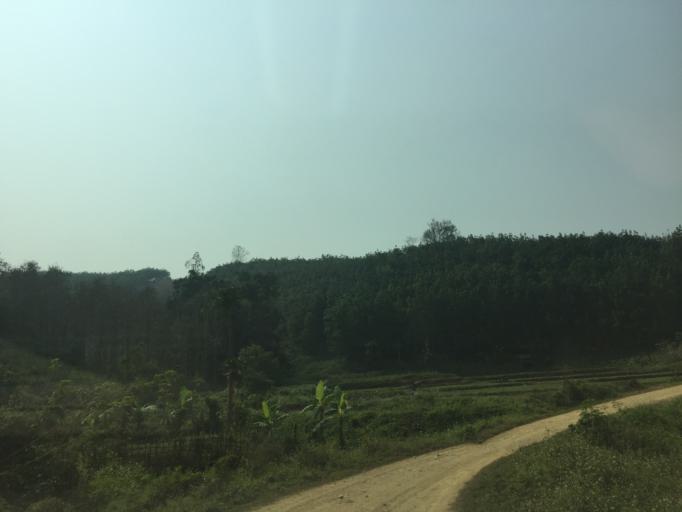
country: TH
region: Phayao
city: Phu Sang
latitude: 19.6286
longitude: 100.5372
